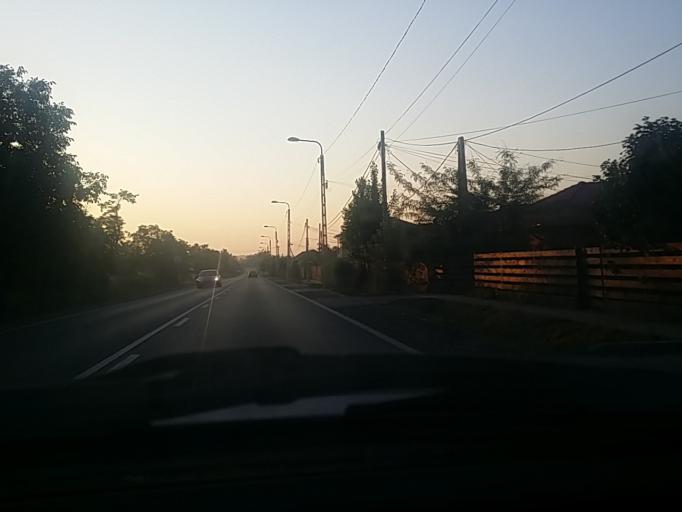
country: HU
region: Pest
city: Maglod
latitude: 47.4471
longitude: 19.3672
